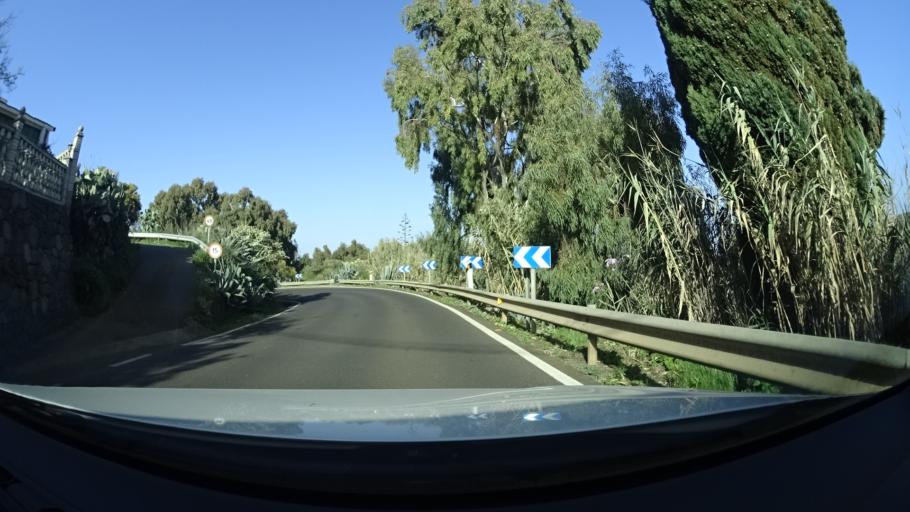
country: ES
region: Canary Islands
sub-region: Provincia de Las Palmas
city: Vega de San Mateo
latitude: 28.0171
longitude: -15.5396
